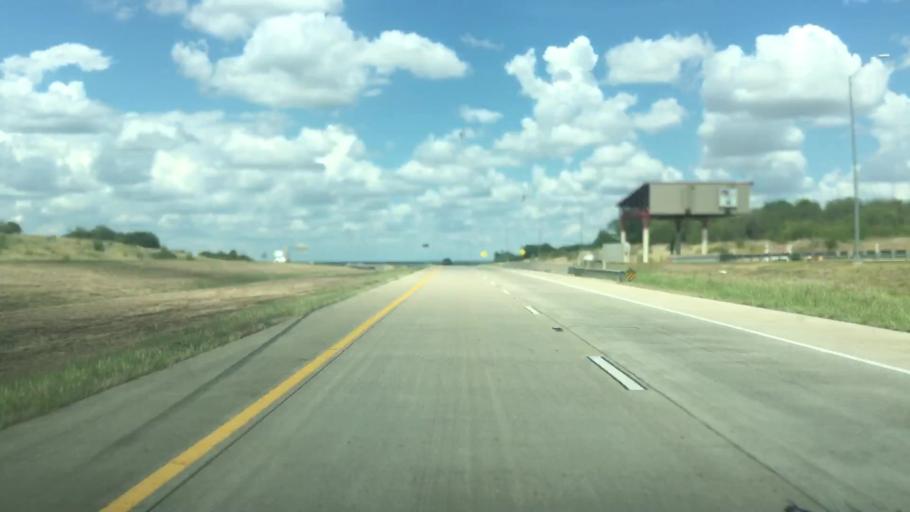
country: US
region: Texas
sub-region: Williamson County
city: Georgetown
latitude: 30.6448
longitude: -97.6311
